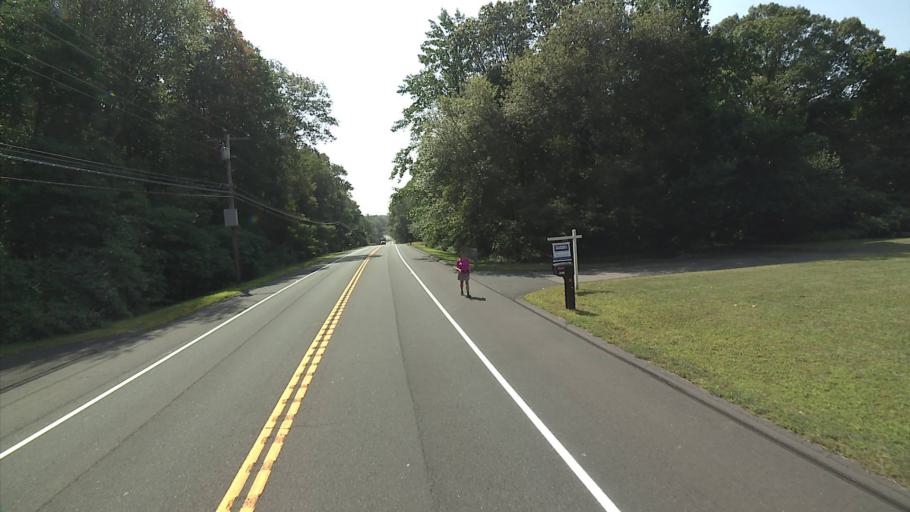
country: US
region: Connecticut
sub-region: New Haven County
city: Guilford
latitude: 41.3664
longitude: -72.6378
